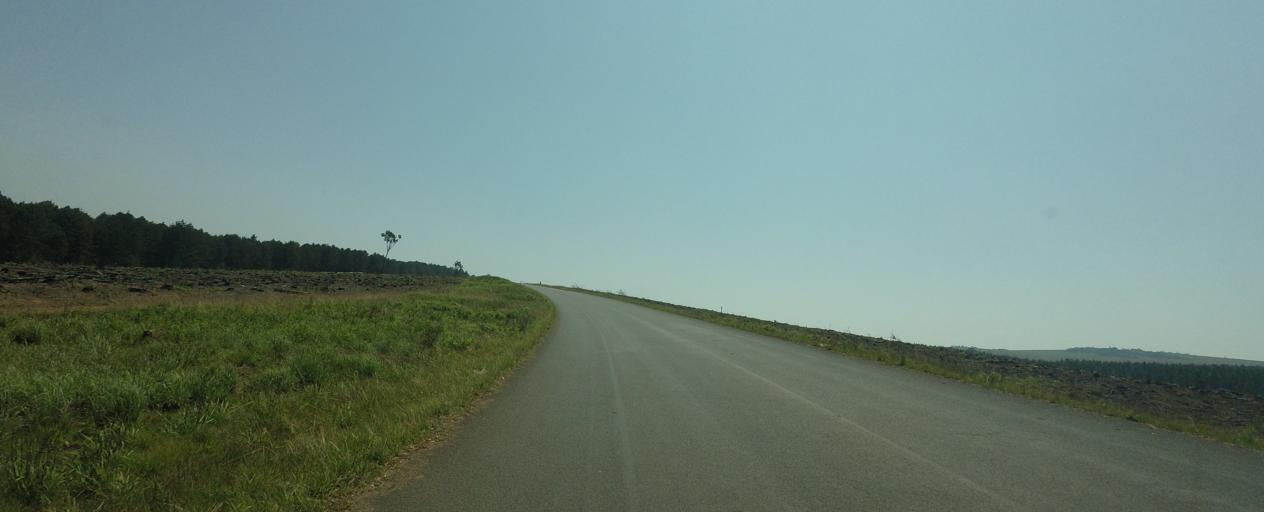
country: ZA
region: Mpumalanga
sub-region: Ehlanzeni District
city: Graksop
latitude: -25.0227
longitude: 30.8227
